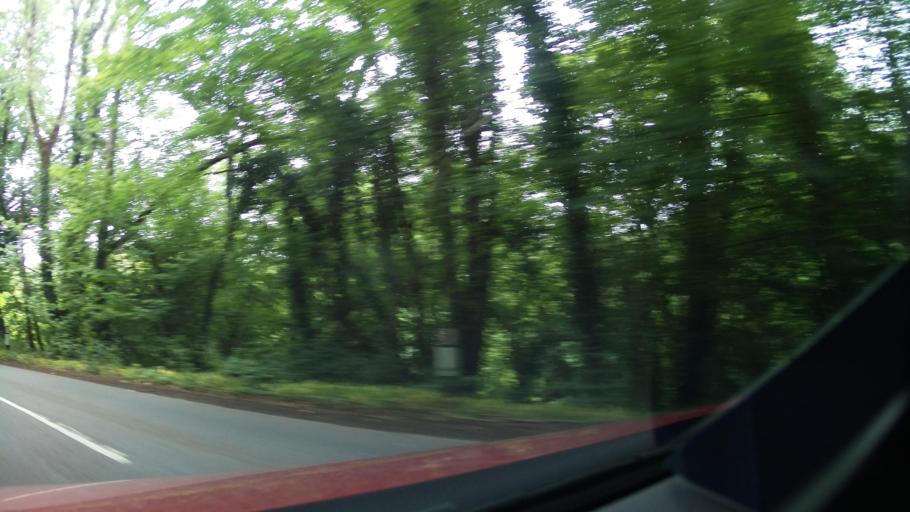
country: GB
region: England
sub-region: Devon
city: Chudleigh
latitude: 50.6409
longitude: -3.6367
